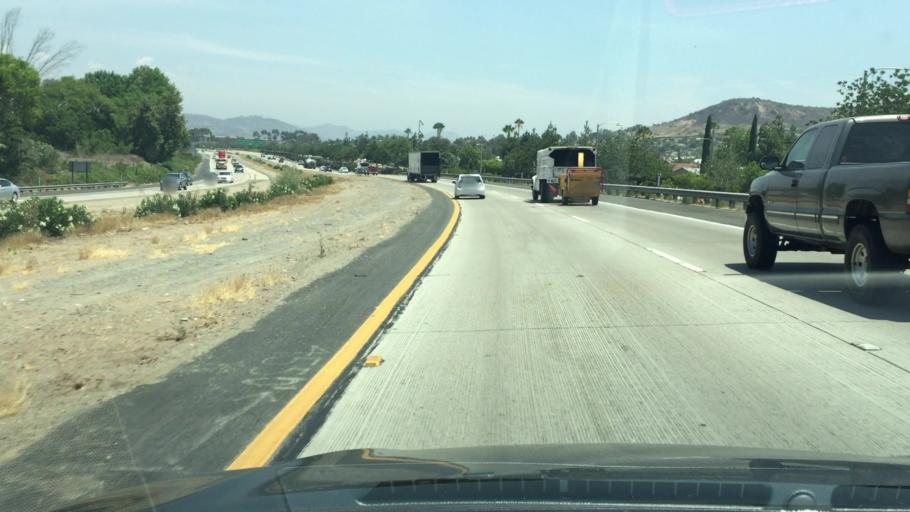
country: US
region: California
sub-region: San Diego County
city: Santee
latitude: 32.8365
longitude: -117.0195
